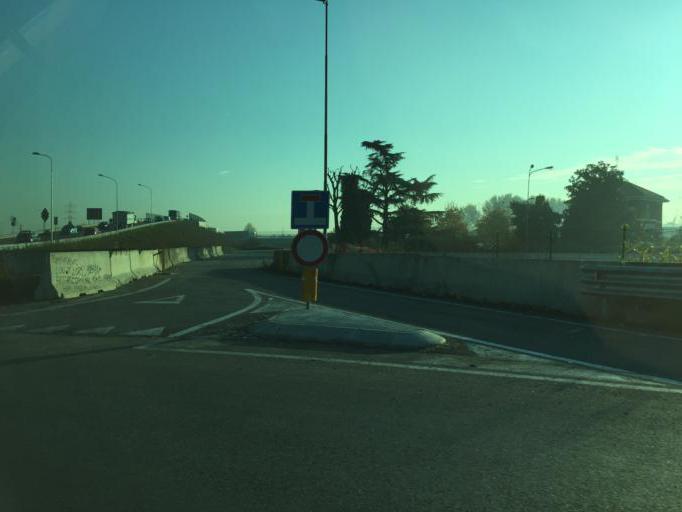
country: IT
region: Lombardy
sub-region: Citta metropolitana di Milano
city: Liscate
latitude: 45.4803
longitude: 9.4270
